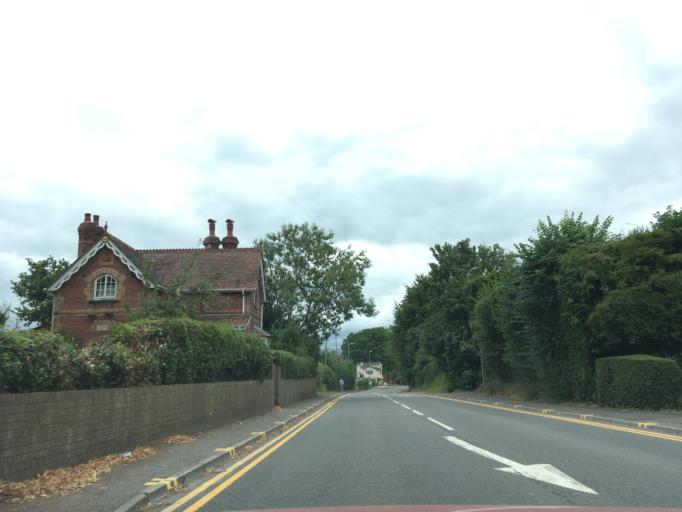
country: GB
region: Wales
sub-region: Monmouthshire
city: Abergavenny
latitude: 51.8262
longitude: -3.0352
